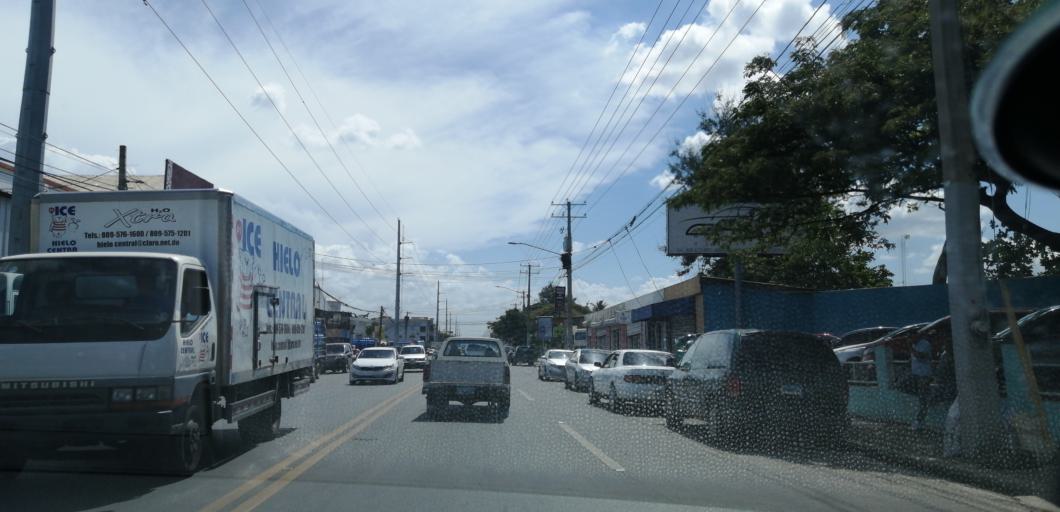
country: DO
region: Santiago
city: Santiago de los Caballeros
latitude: 19.4877
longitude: -70.7167
